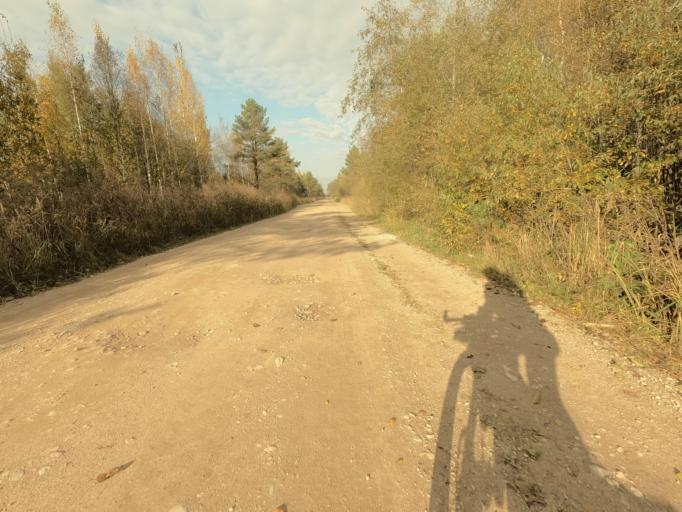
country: RU
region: Novgorod
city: Volkhovskiy
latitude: 58.8964
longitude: 31.0303
